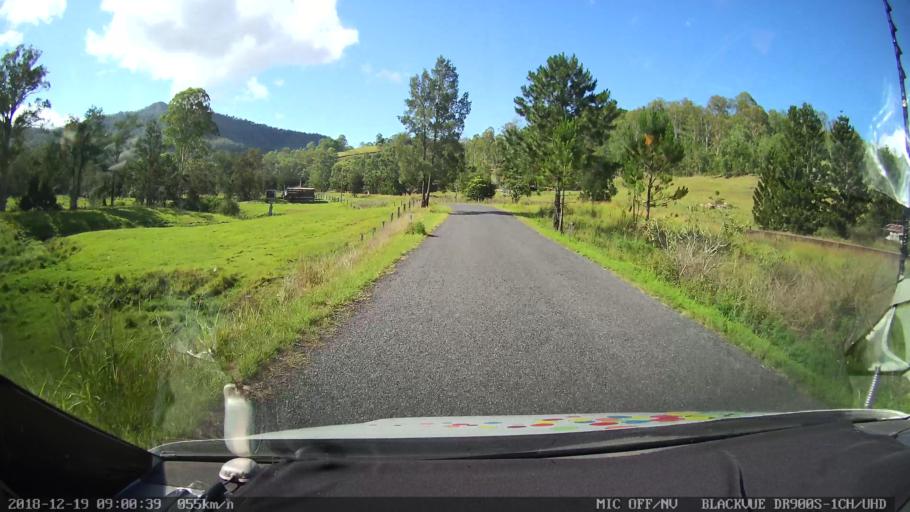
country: AU
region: New South Wales
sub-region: Kyogle
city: Kyogle
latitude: -28.4336
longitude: 152.9567
